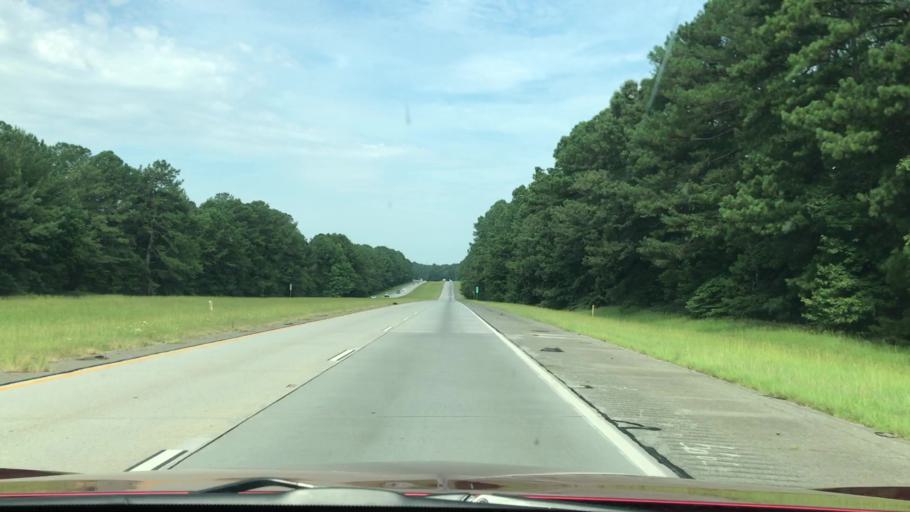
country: US
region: Georgia
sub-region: Warren County
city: Firing Range
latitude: 33.5042
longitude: -82.7561
